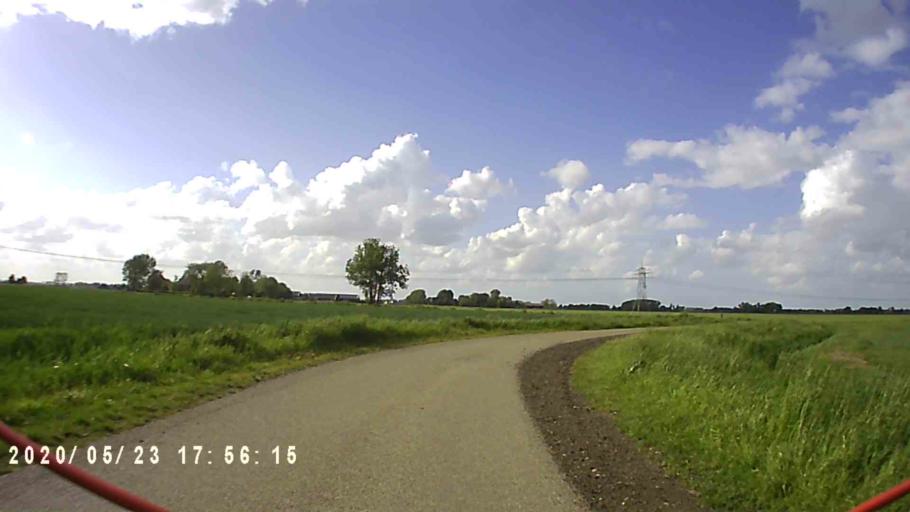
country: NL
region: Groningen
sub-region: Gemeente Slochteren
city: Slochteren
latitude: 53.2500
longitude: 6.7453
